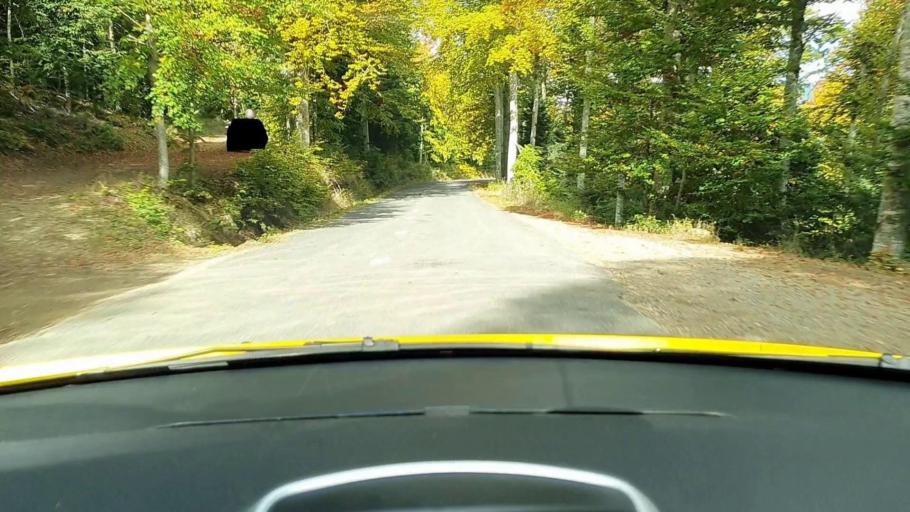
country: FR
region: Languedoc-Roussillon
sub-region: Departement du Gard
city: Valleraugue
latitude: 44.0721
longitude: 3.5679
